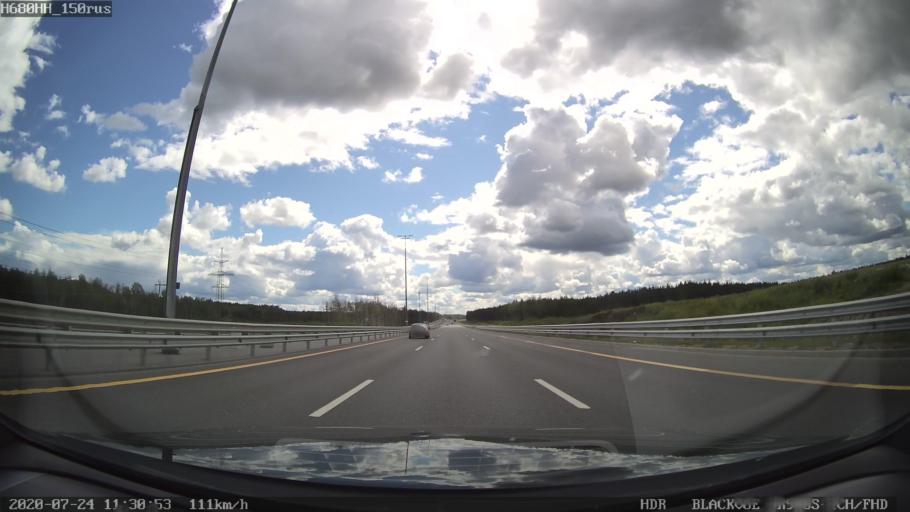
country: RU
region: Leningrad
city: Krasnyy Bor
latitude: 59.6647
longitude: 30.6220
